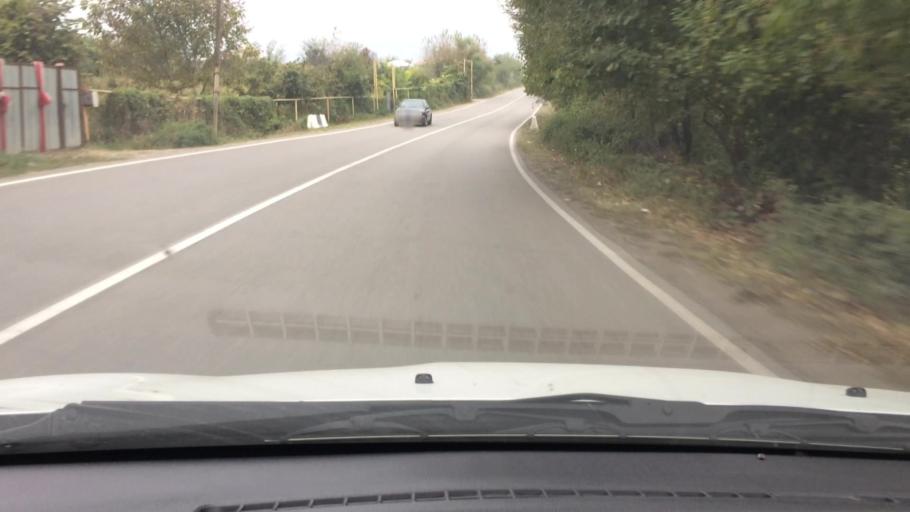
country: AM
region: Tavush
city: Bagratashen
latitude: 41.2342
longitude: 44.8113
